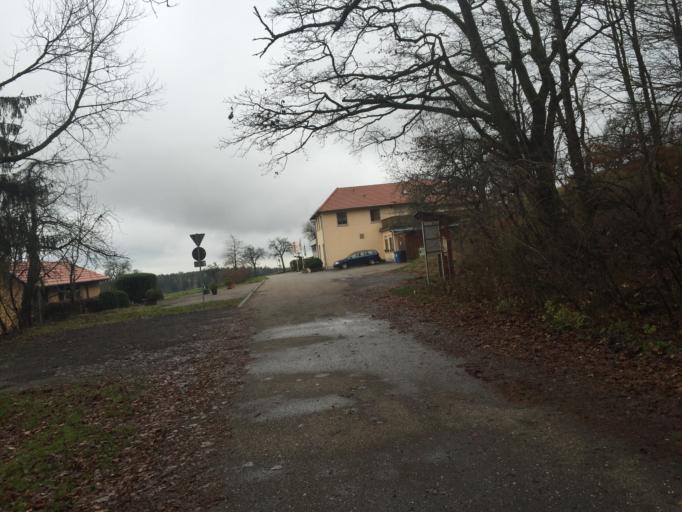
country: DE
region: Baden-Wuerttemberg
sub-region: Karlsruhe Region
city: Zwingenberg
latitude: 49.4679
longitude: 9.0458
